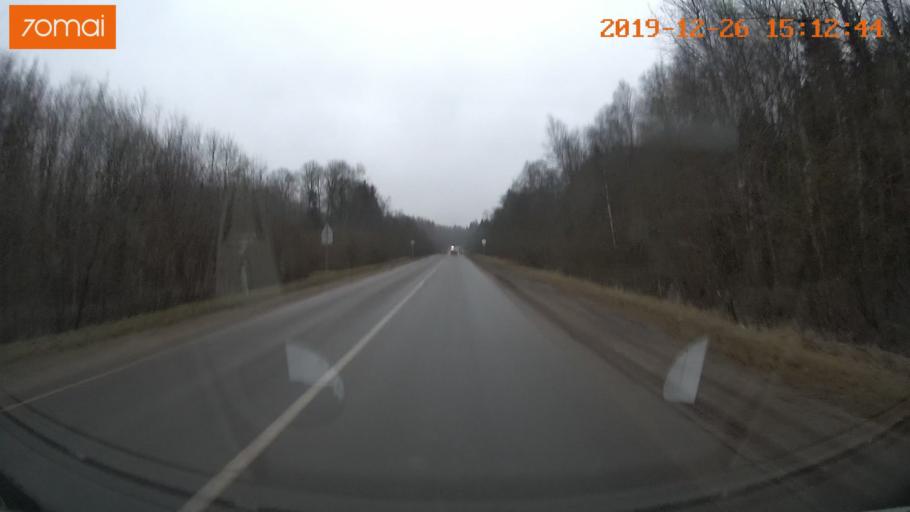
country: RU
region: Jaroslavl
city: Rybinsk
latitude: 58.1254
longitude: 38.8798
